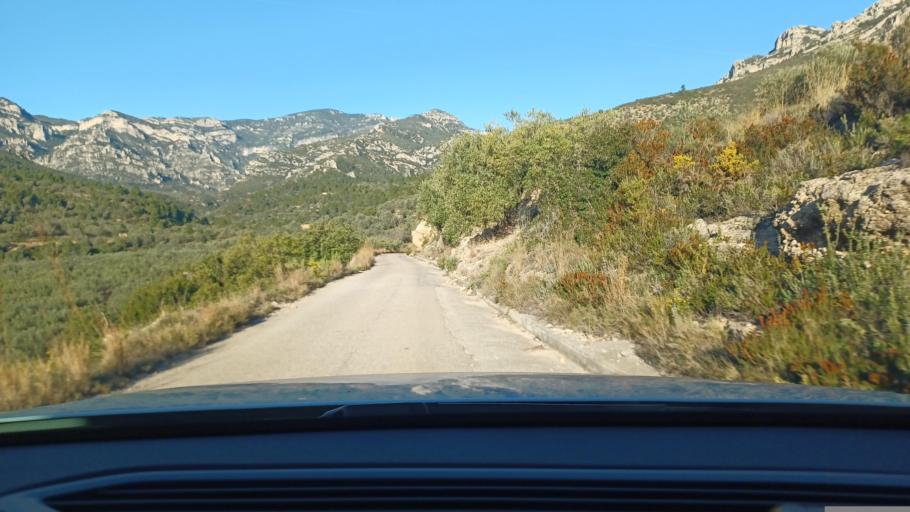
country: ES
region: Catalonia
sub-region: Provincia de Tarragona
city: Mas de Barberans
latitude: 40.7185
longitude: 0.3512
